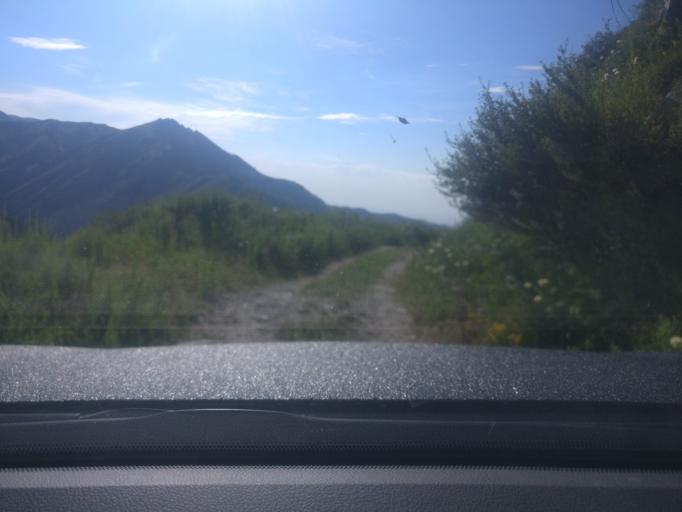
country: KZ
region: Almaty Qalasy
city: Almaty
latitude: 43.1068
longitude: 76.9348
